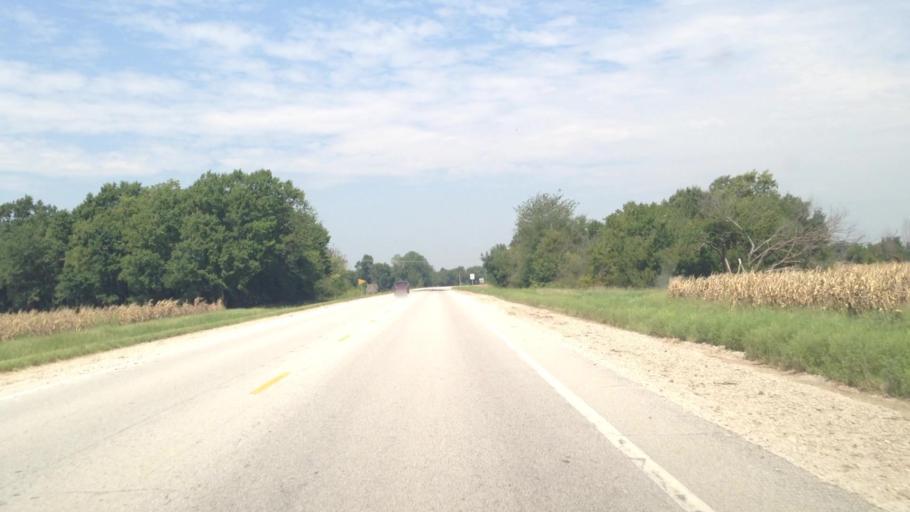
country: US
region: Kansas
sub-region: Labette County
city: Parsons
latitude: 37.3871
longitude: -95.2660
